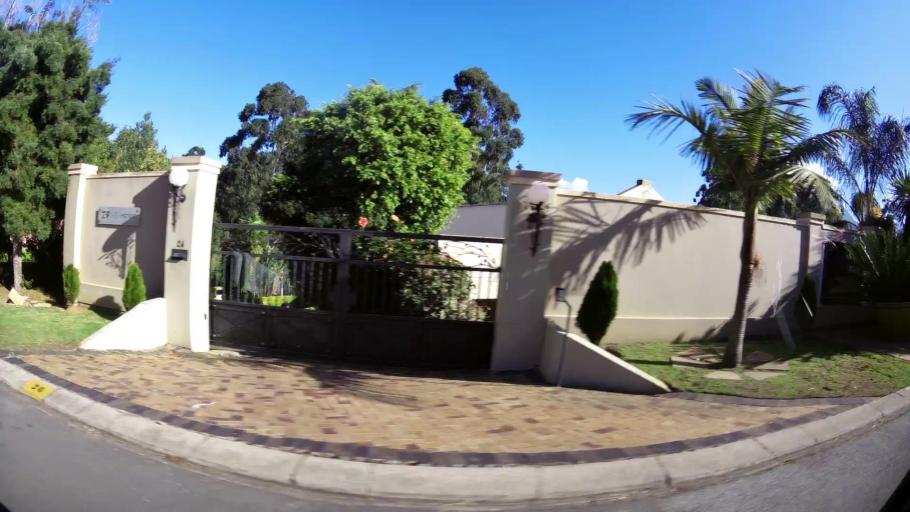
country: ZA
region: Western Cape
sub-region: Eden District Municipality
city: George
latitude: -33.9572
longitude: 22.4204
